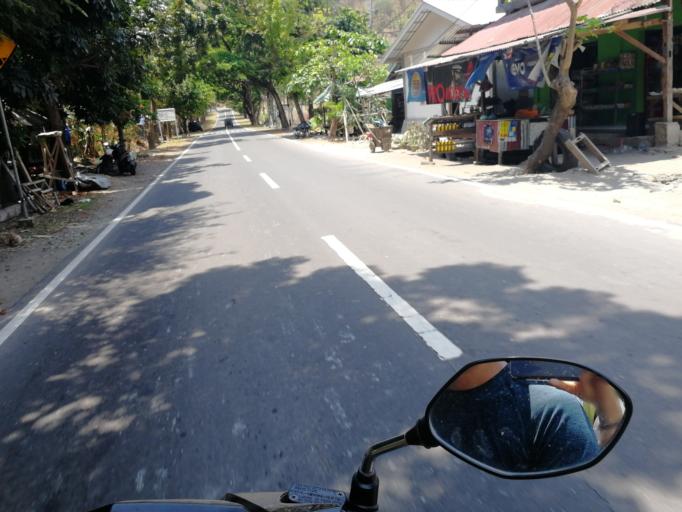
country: ID
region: West Nusa Tenggara
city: Karangsubagan
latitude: -8.4425
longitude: 116.0421
